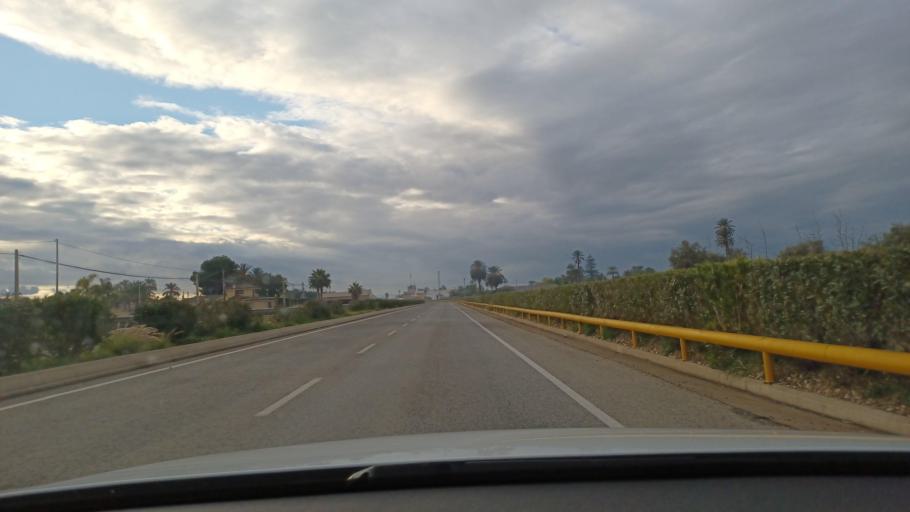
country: ES
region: Valencia
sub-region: Provincia de Alicante
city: Elche
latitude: 38.2280
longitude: -0.6994
